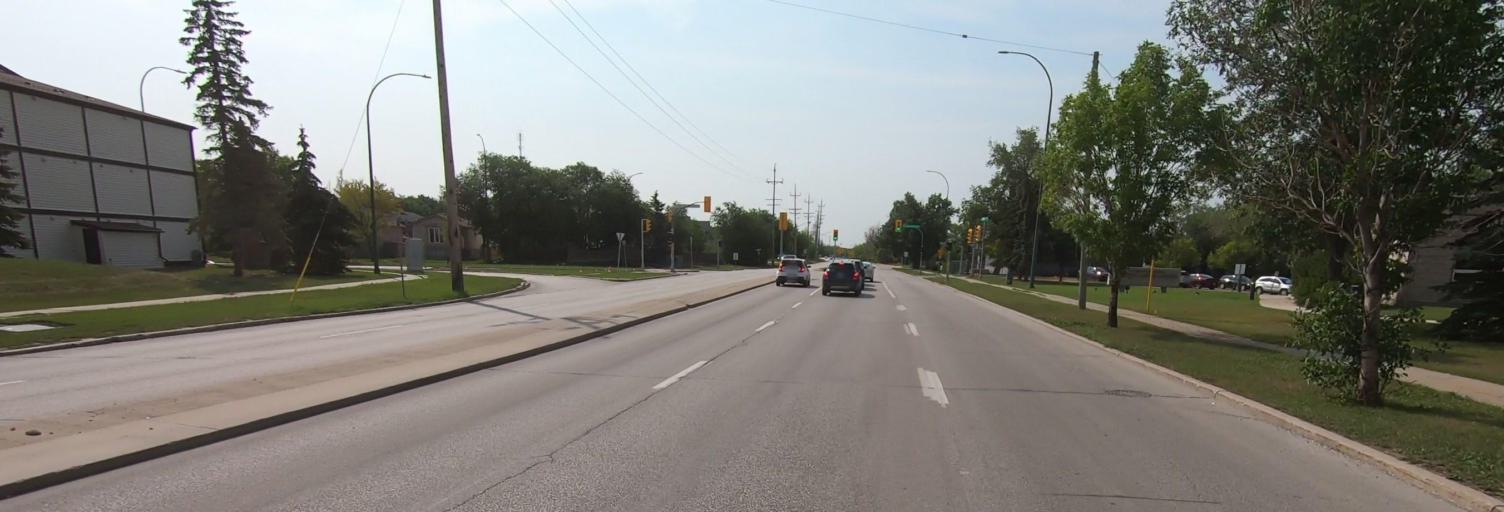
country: CA
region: Manitoba
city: Winnipeg
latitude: 49.8021
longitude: -97.1161
